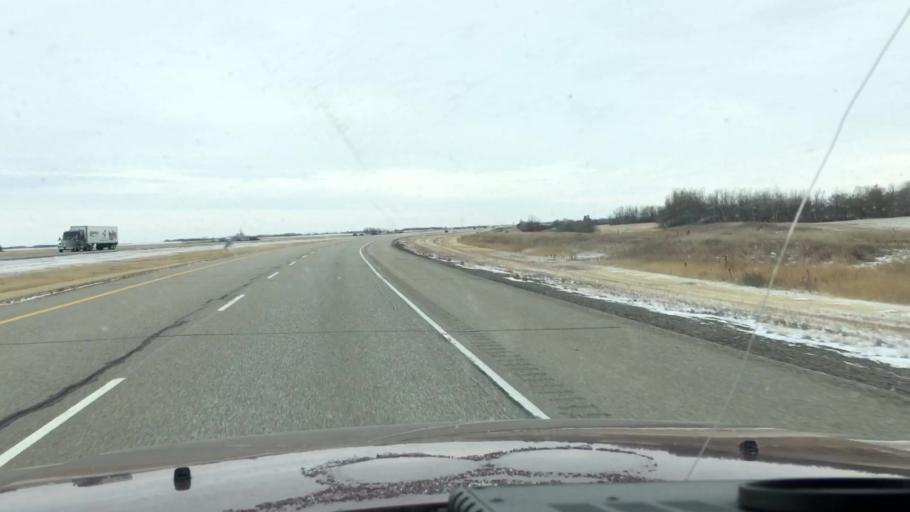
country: CA
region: Saskatchewan
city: Watrous
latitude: 51.3353
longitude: -106.0872
